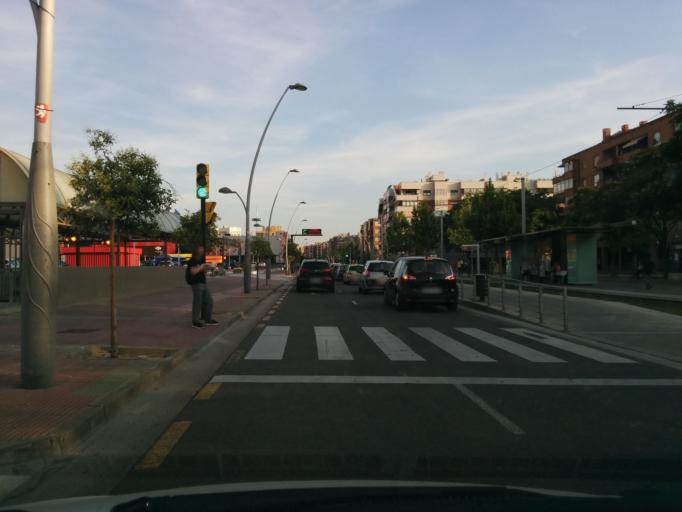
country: ES
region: Aragon
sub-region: Provincia de Zaragoza
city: Almozara
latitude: 41.6780
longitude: -0.8906
